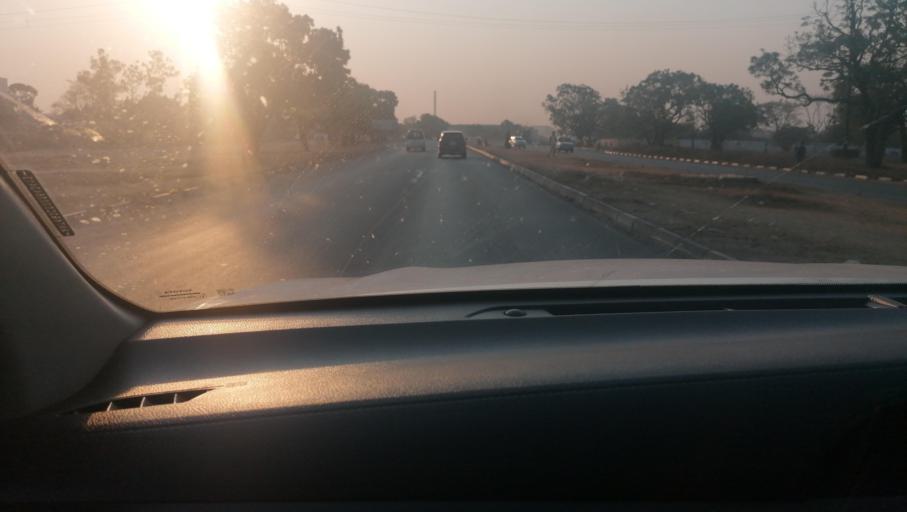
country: ZM
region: Copperbelt
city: Kitwe
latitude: -12.8445
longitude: 28.2168
